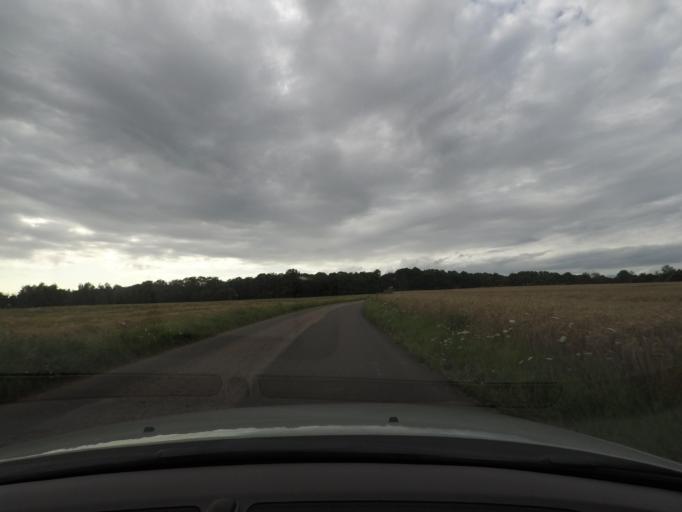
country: FR
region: Haute-Normandie
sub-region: Departement de l'Eure
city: Le Manoir
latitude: 49.3303
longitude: 1.2092
